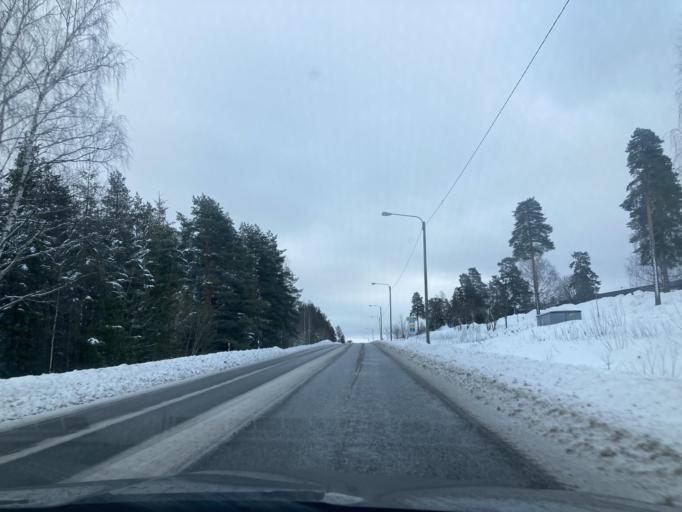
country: FI
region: Paijanne Tavastia
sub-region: Lahti
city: Asikkala
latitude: 61.1667
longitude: 25.5624
